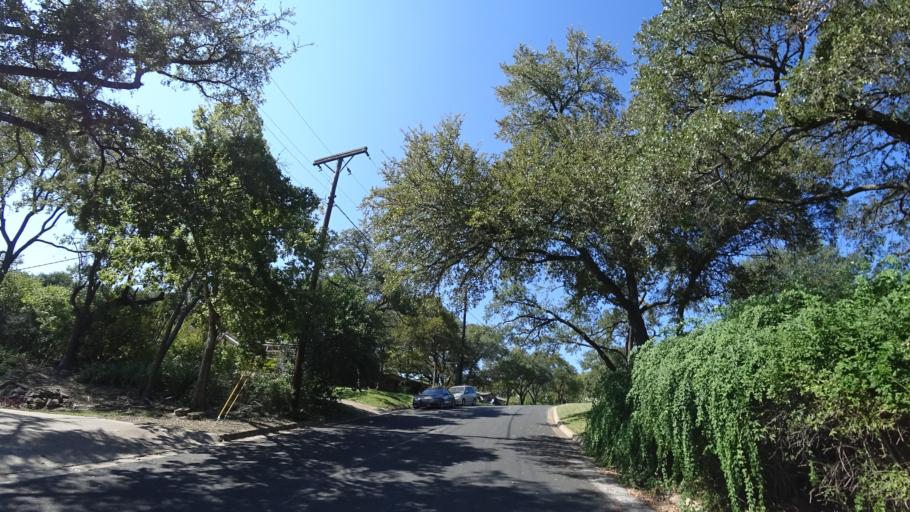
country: US
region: Texas
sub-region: Travis County
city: Rollingwood
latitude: 30.2460
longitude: -97.7868
